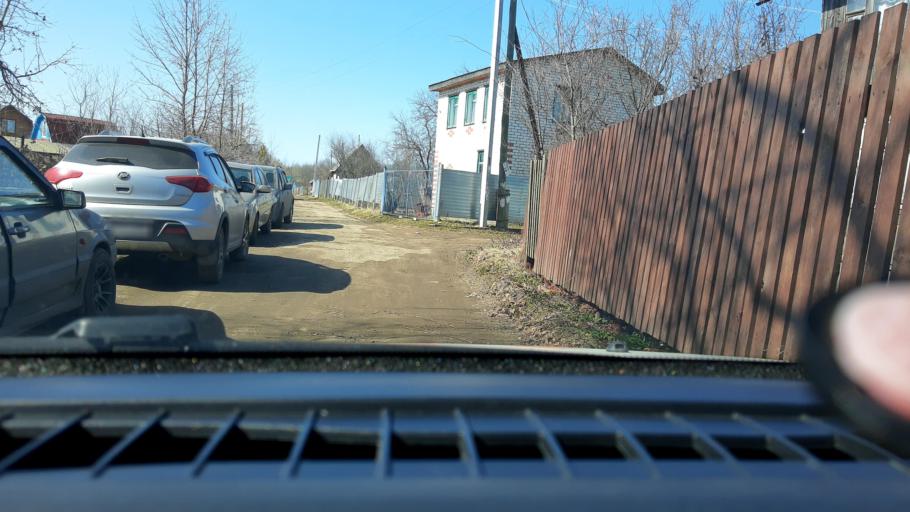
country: RU
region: Nizjnij Novgorod
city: Gorbatovka
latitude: 56.2644
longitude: 43.8221
